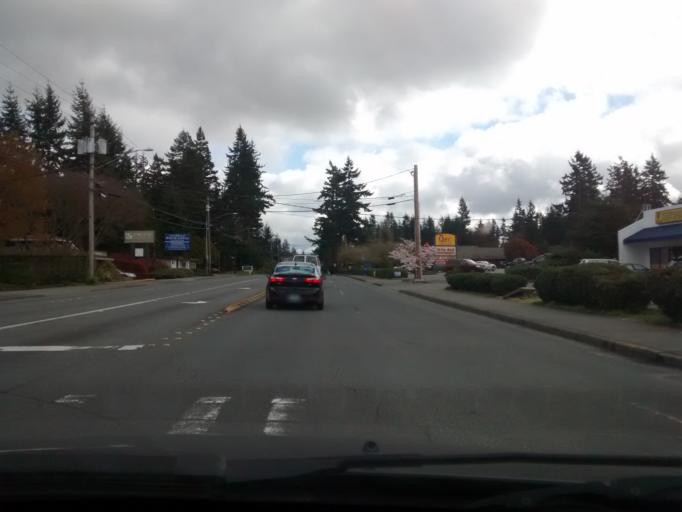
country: US
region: Washington
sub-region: Snohomish County
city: Lynnwood
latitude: 47.8214
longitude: -122.3359
